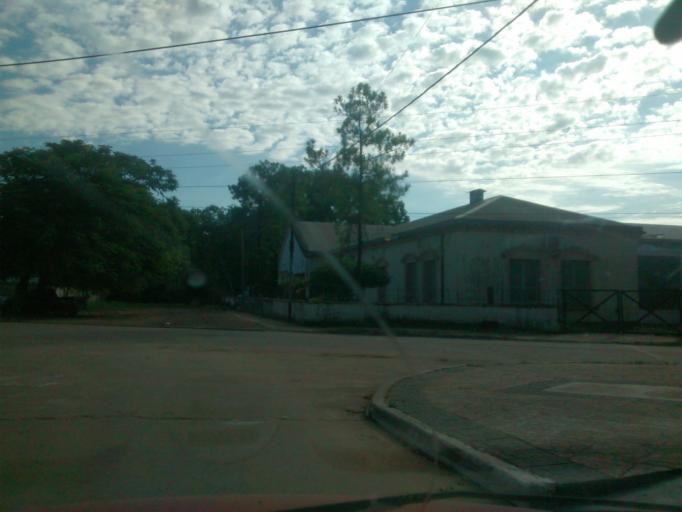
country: AR
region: Chaco
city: Puerto Tirol
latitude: -27.3751
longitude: -59.0871
